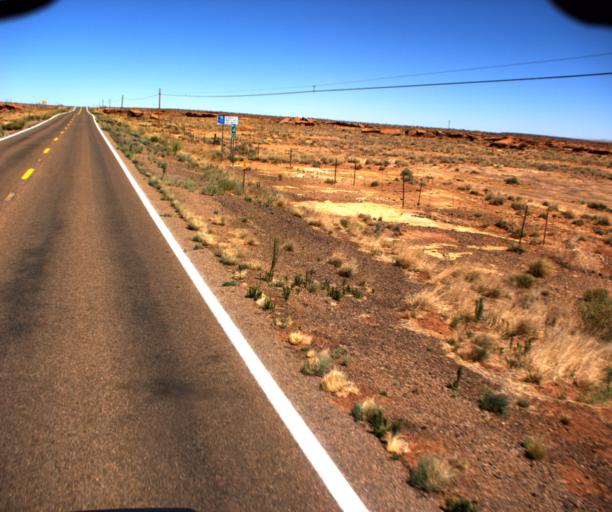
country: US
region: Arizona
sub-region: Navajo County
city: Winslow
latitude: 34.9880
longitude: -110.6650
